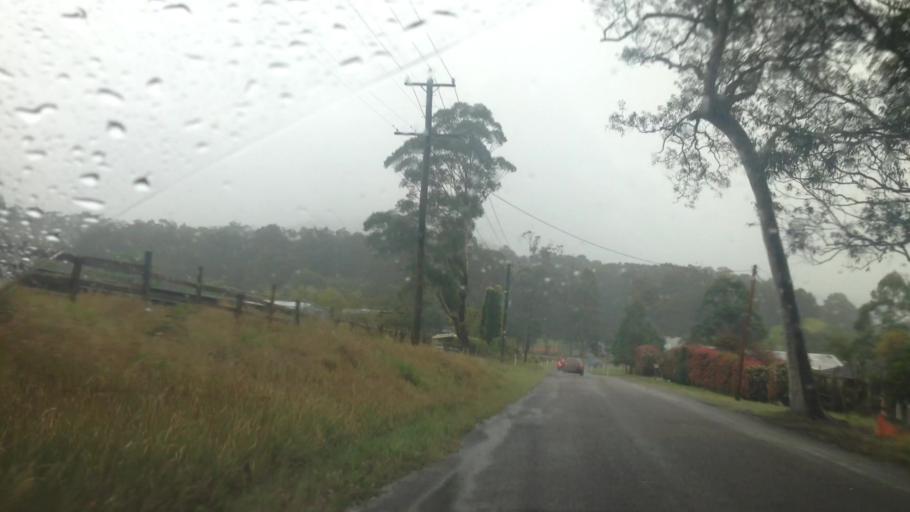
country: AU
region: New South Wales
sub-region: Wyong Shire
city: Little Jilliby
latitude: -33.1919
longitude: 151.3560
